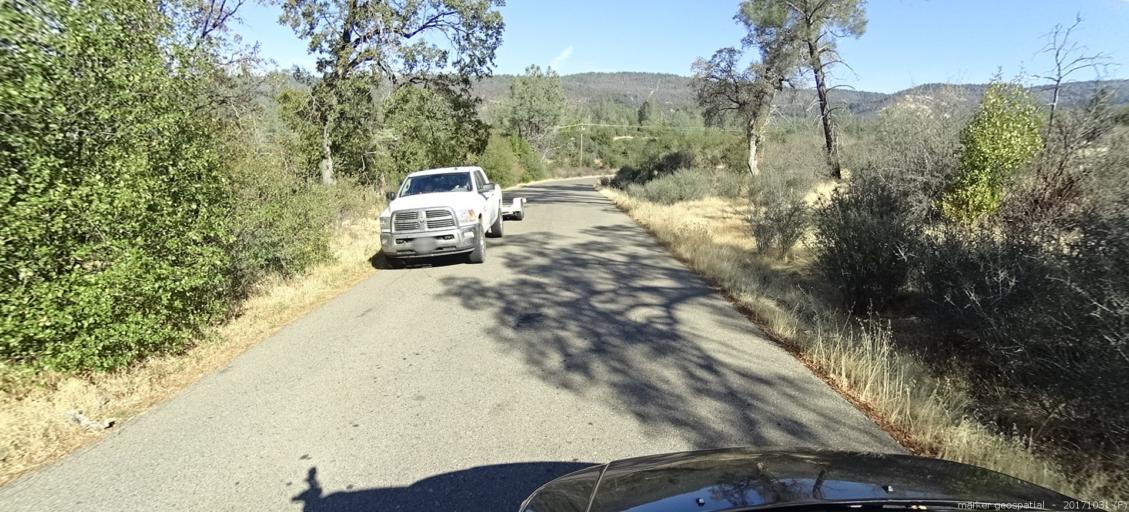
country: US
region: California
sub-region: Shasta County
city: Shingletown
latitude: 40.4423
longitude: -121.8712
